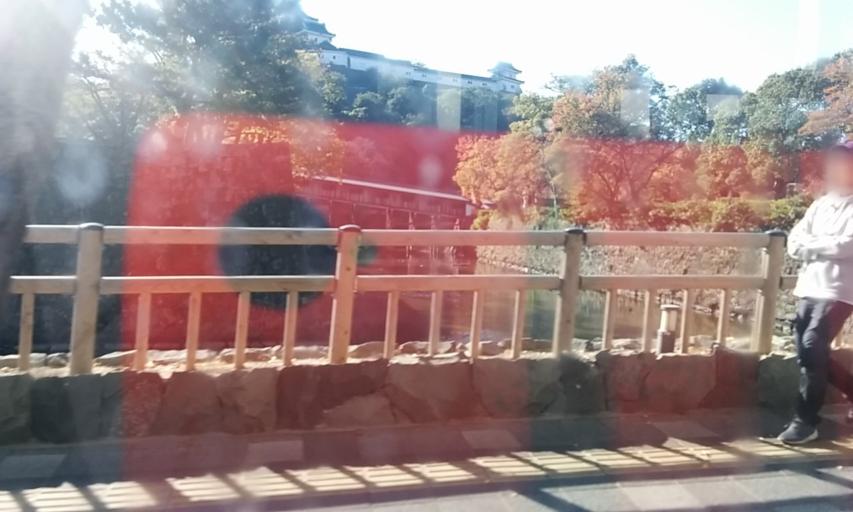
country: JP
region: Wakayama
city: Wakayama-shi
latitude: 34.2298
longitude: 135.1716
